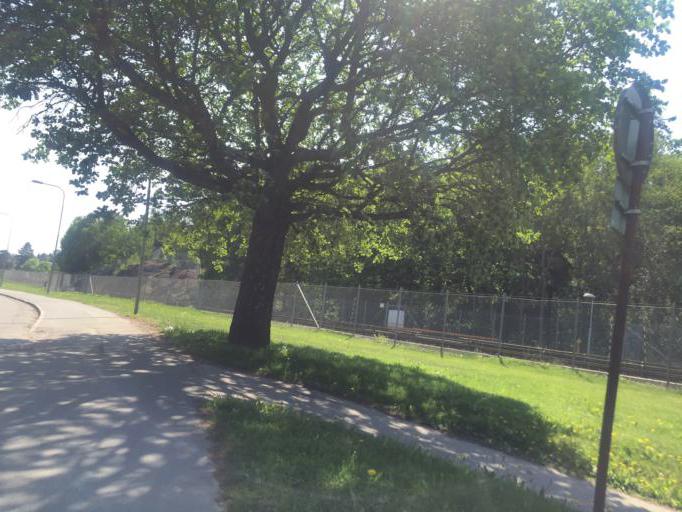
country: SE
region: Stockholm
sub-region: Stockholms Kommun
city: Arsta
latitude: 59.2808
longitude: 18.0693
